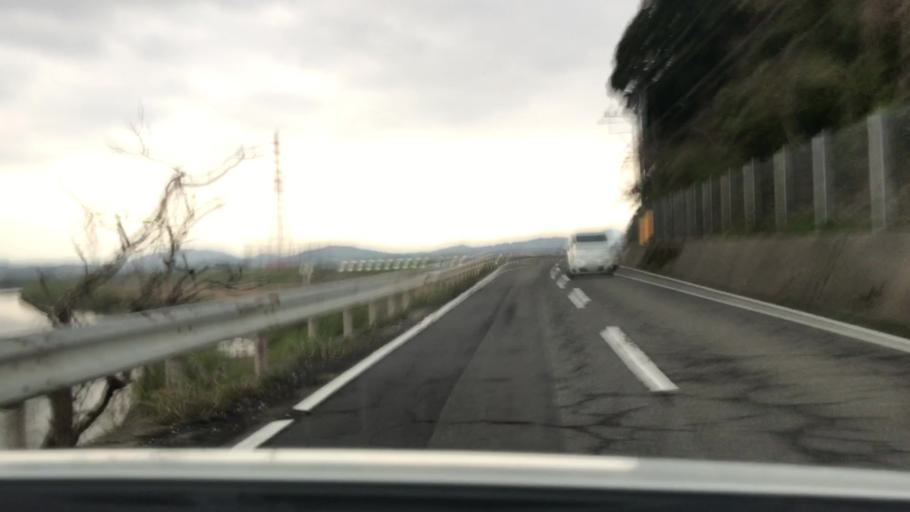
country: JP
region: Fukui
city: Fukui-shi
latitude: 36.0826
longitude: 136.1800
